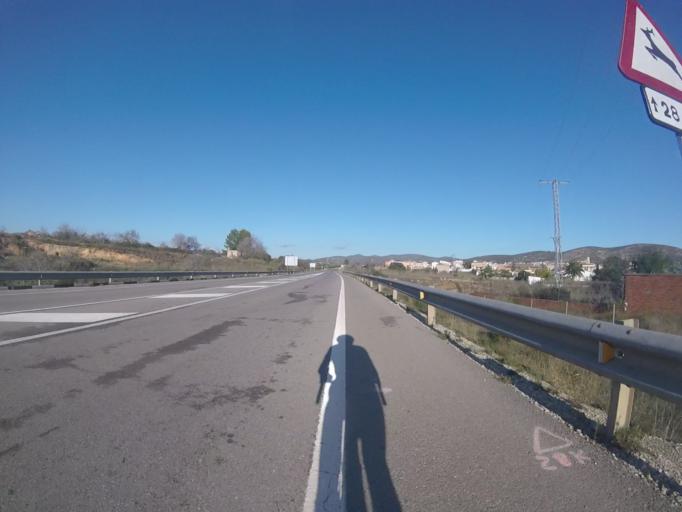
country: ES
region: Valencia
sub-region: Provincia de Castello
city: Cuevas de Vinroma
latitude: 40.3076
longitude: 0.1141
